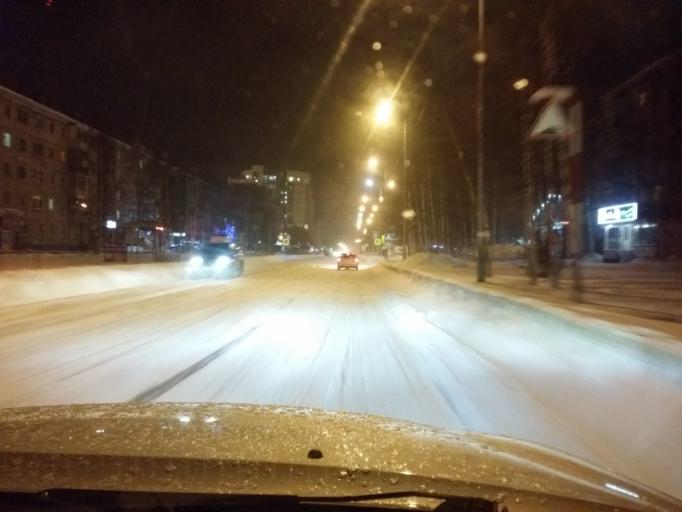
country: RU
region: Khanty-Mansiyskiy Avtonomnyy Okrug
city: Nizhnevartovsk
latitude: 60.9415
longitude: 76.5795
